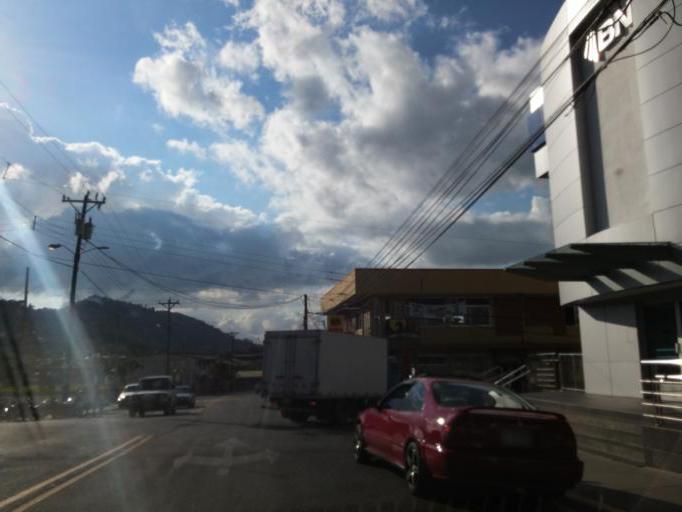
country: CR
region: San Jose
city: San Ignacio
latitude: 9.7990
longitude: -84.1621
